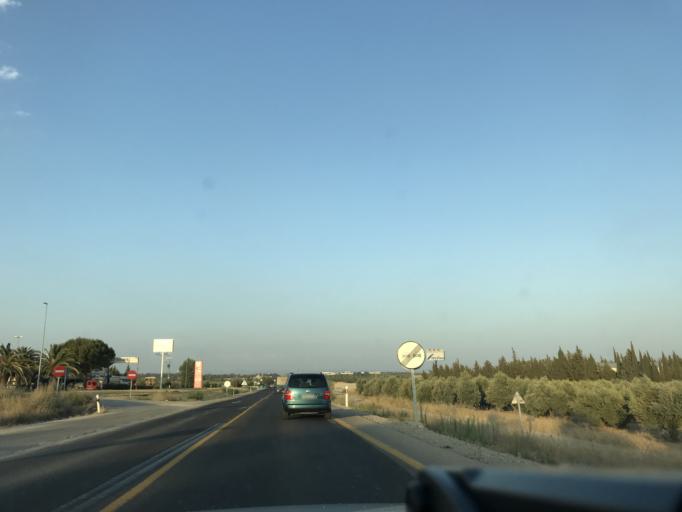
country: ES
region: Andalusia
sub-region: Provincia de Jaen
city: Ubeda
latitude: 38.0306
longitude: -3.3351
